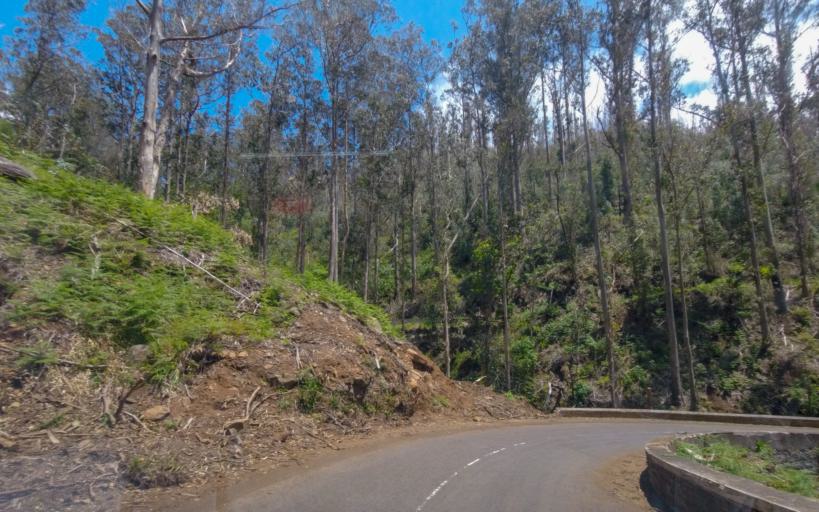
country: PT
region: Madeira
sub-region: Funchal
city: Nossa Senhora do Monte
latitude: 32.6803
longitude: -16.8801
